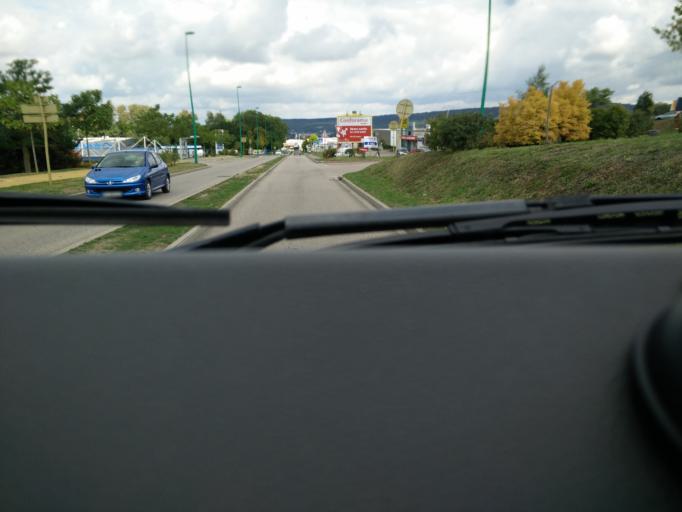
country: FR
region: Lorraine
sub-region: Departement de la Meuse
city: Verdun
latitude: 49.1421
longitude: 5.4098
